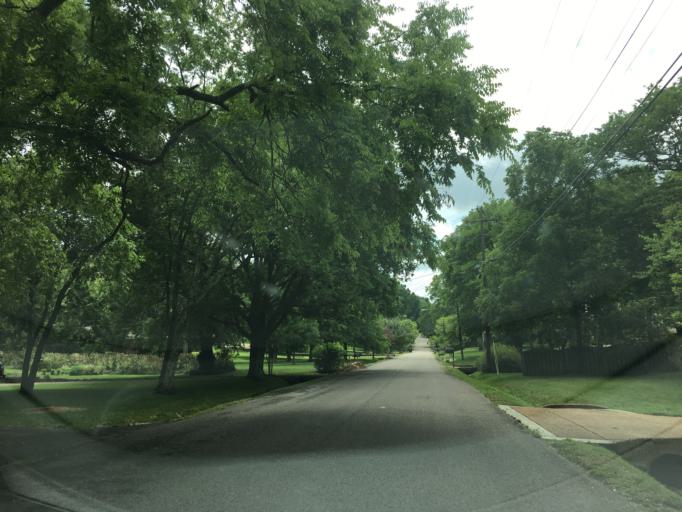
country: US
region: Tennessee
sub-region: Davidson County
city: Belle Meade
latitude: 36.0907
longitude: -86.8458
